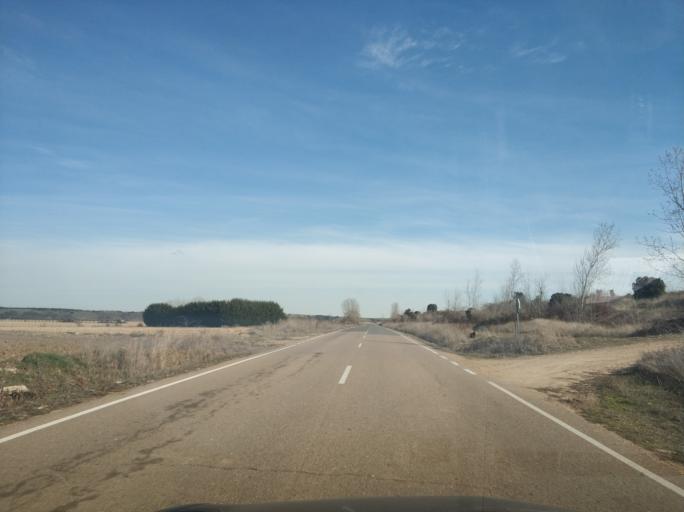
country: ES
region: Castille and Leon
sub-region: Provincia de Salamanca
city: Valverdon
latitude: 41.0381
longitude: -5.7841
